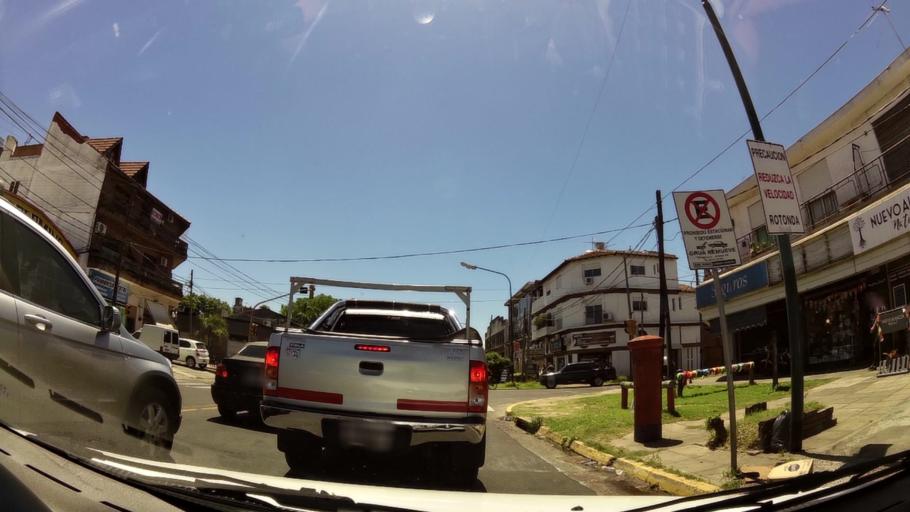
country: AR
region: Buenos Aires
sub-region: Partido de San Isidro
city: San Isidro
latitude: -34.4908
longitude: -58.5240
